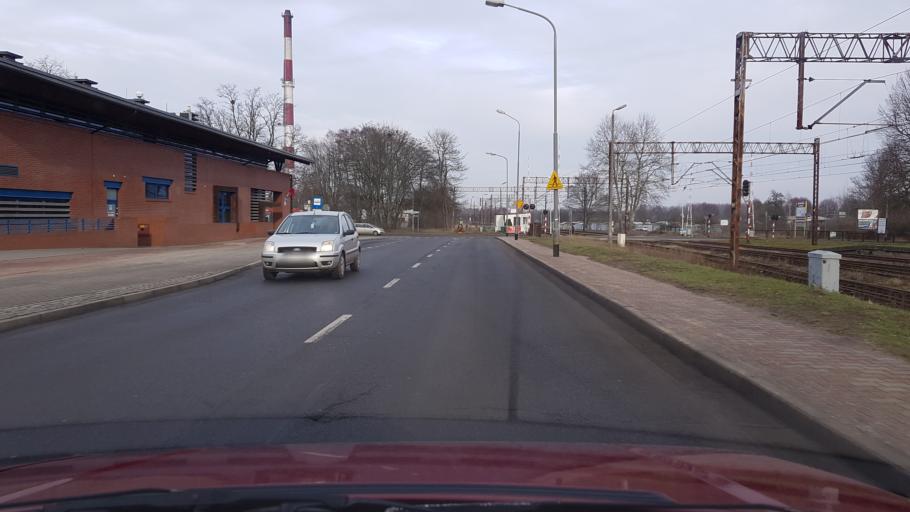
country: PL
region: West Pomeranian Voivodeship
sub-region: Powiat policki
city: Police
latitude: 53.5502
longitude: 14.5653
